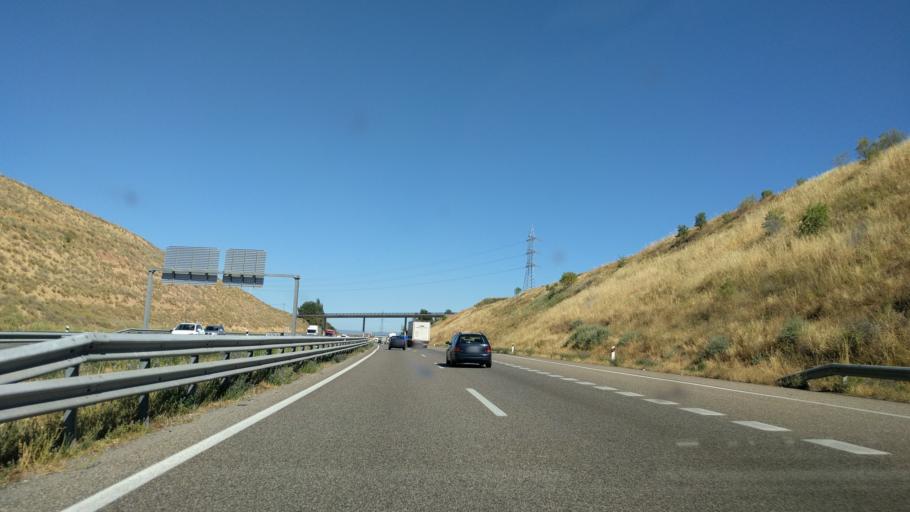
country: ES
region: Catalonia
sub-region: Provincia de Lleida
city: Alcoletge
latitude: 41.6376
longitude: 0.6819
